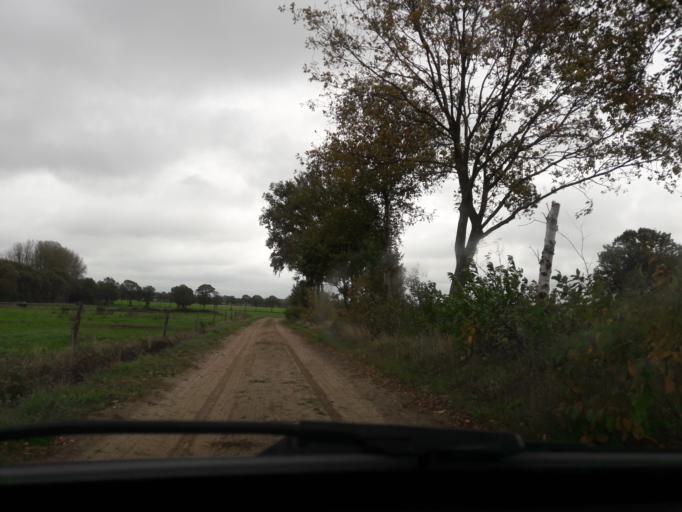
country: NL
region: Drenthe
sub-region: Gemeente Borger-Odoorn
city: Borger
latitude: 52.9355
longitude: 6.8005
